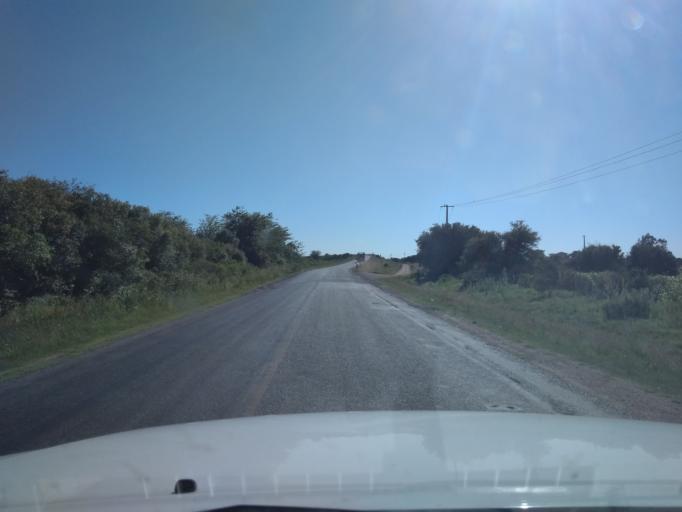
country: UY
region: Canelones
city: San Ramon
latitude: -34.2679
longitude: -55.9344
